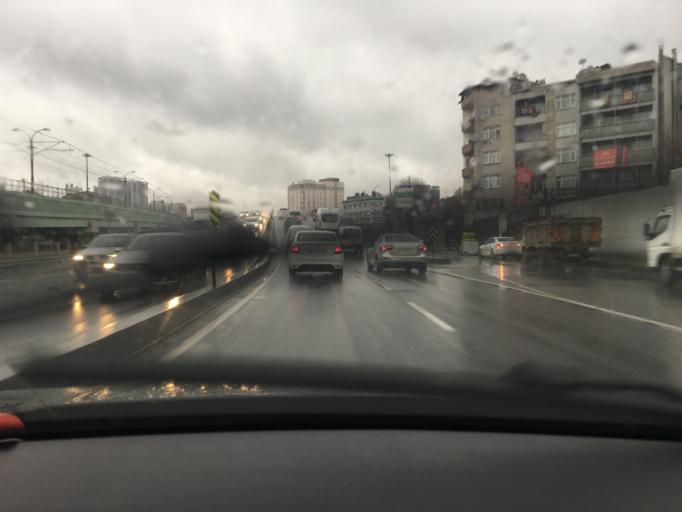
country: TR
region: Istanbul
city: merter keresteciler
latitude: 41.0327
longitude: 28.8970
